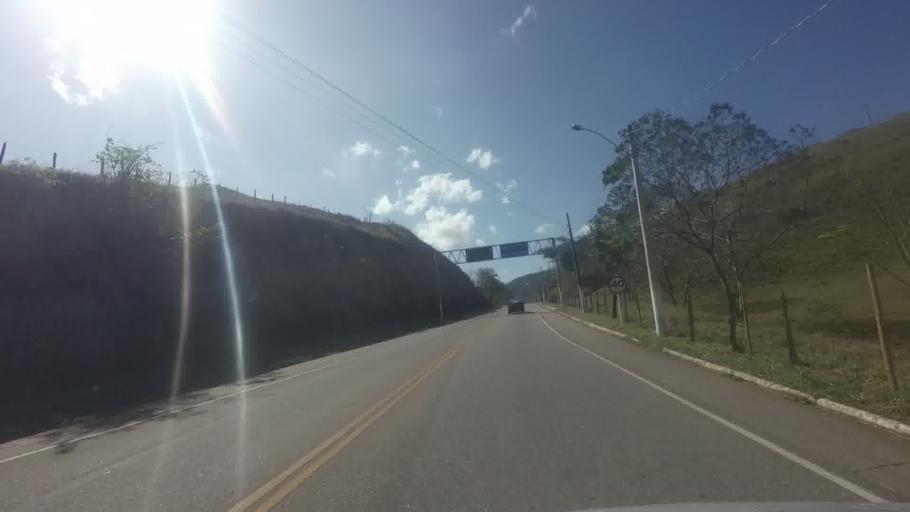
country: BR
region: Rio de Janeiro
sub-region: Bom Jesus Do Itabapoana
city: Bom Jesus do Itabapoana
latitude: -21.1301
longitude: -41.6564
